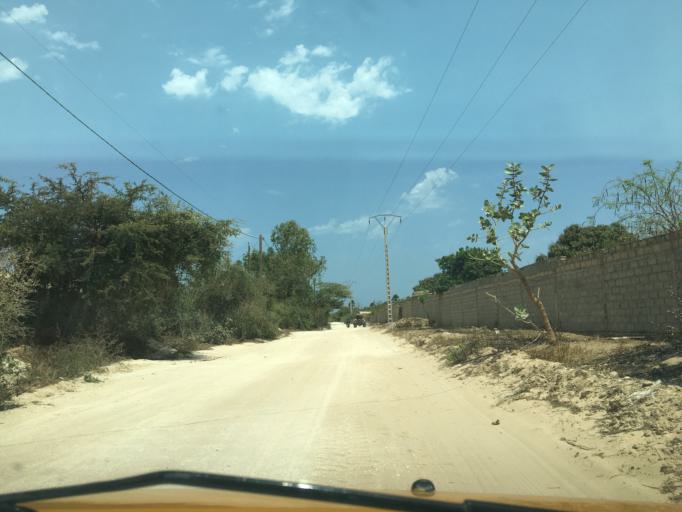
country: SN
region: Thies
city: Thies
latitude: 14.8235
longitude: -17.2042
